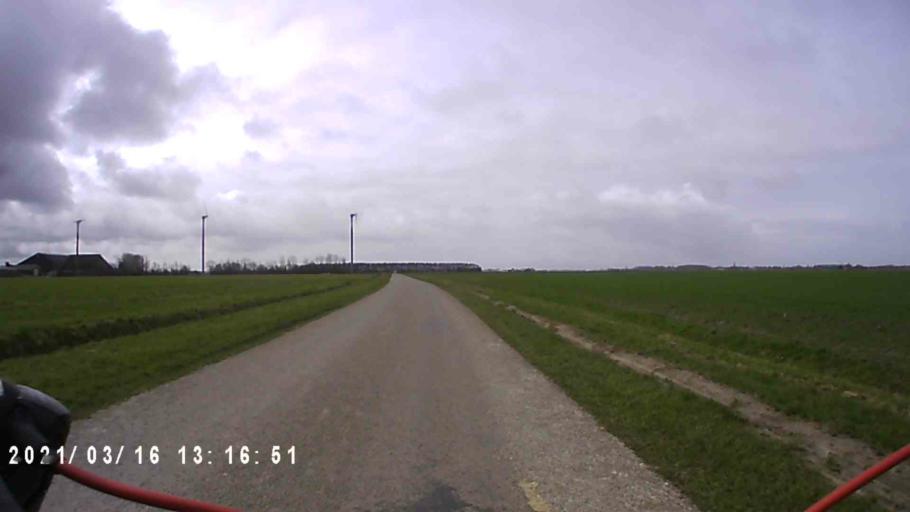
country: NL
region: Friesland
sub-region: Gemeente Het Bildt
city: Minnertsga
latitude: 53.2372
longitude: 5.5927
